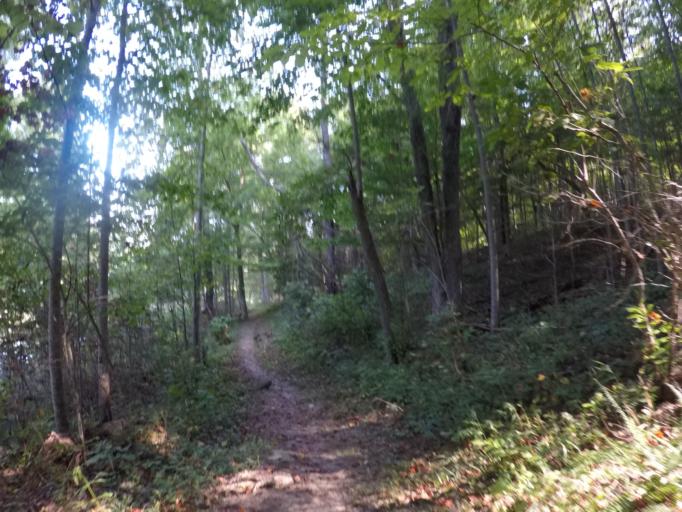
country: US
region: Ohio
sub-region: Lawrence County
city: Ironton
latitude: 38.6151
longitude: -82.6273
